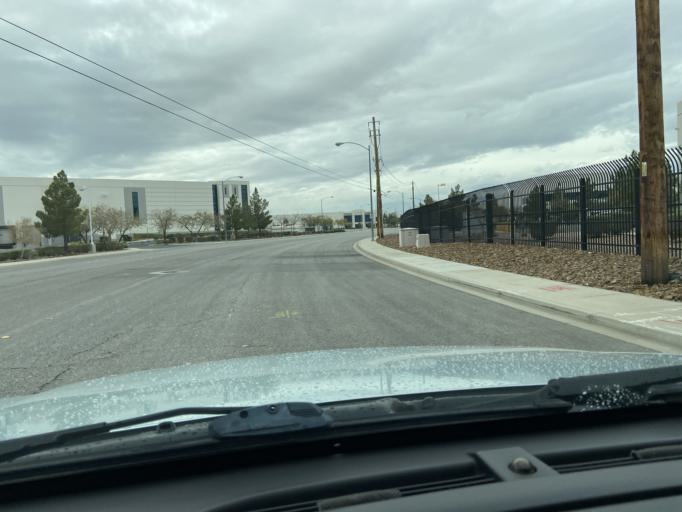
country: US
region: Nevada
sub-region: Clark County
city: Nellis Air Force Base
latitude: 36.2472
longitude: -115.1009
